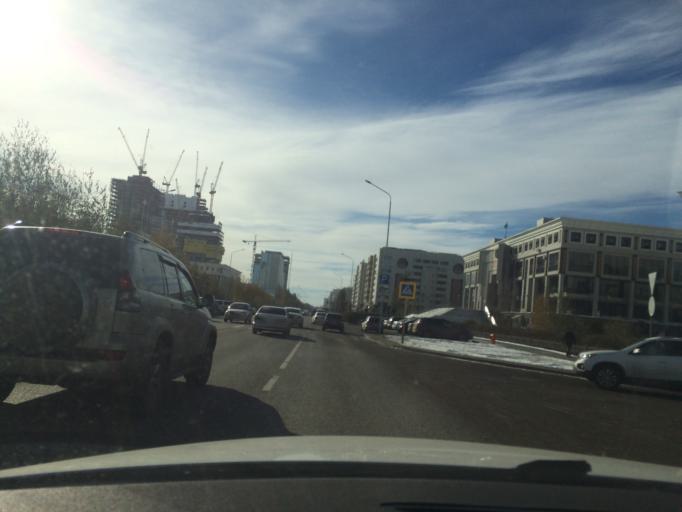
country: KZ
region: Astana Qalasy
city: Astana
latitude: 51.1283
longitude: 71.4284
